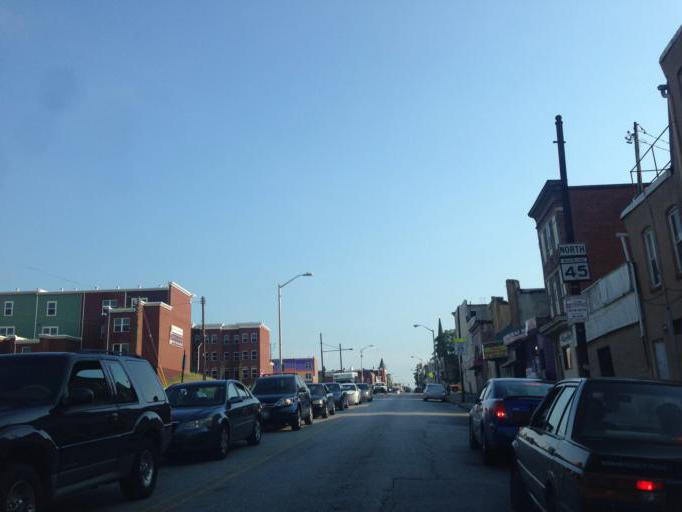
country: US
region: Maryland
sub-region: City of Baltimore
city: Baltimore
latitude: 39.3116
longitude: -76.6094
